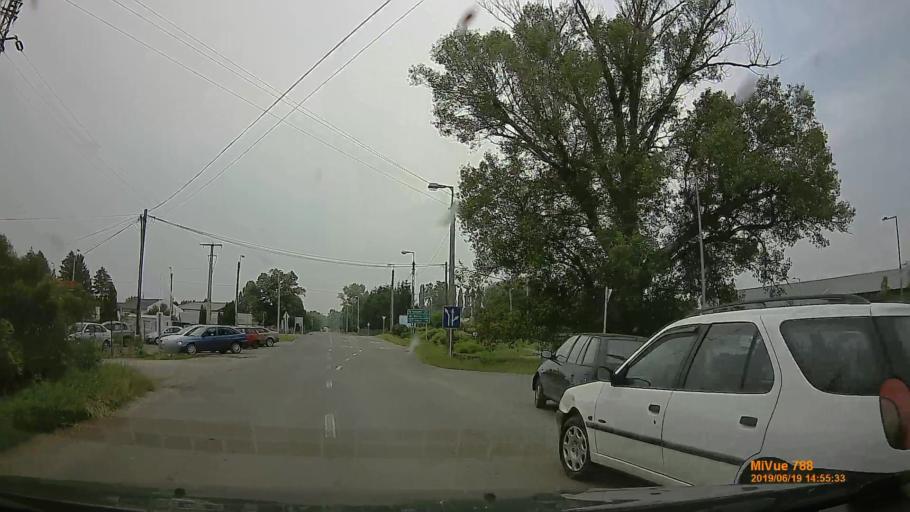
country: HU
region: Baranya
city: Szigetvar
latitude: 46.0426
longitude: 17.8170
